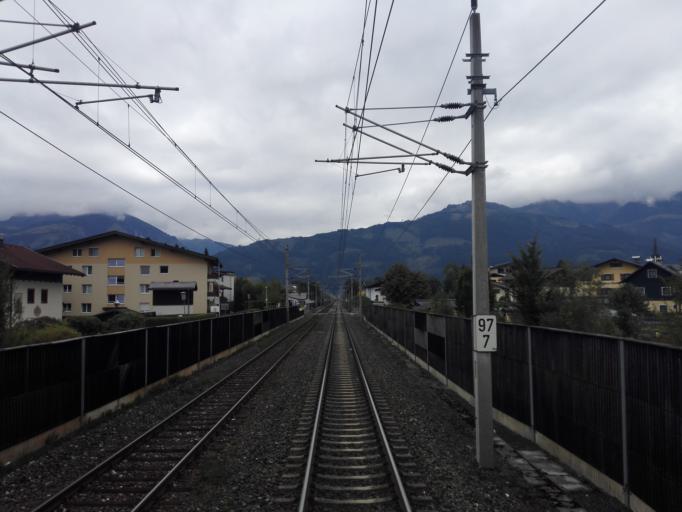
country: AT
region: Salzburg
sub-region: Politischer Bezirk Zell am See
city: Zell am See
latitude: 47.3064
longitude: 12.7946
